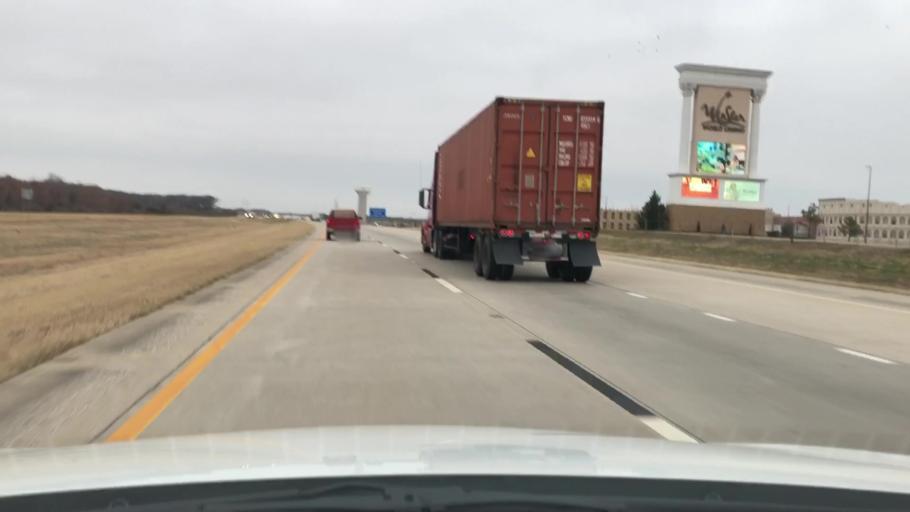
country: US
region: Texas
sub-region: Cooke County
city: Gainesville
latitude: 33.7553
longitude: -97.1349
